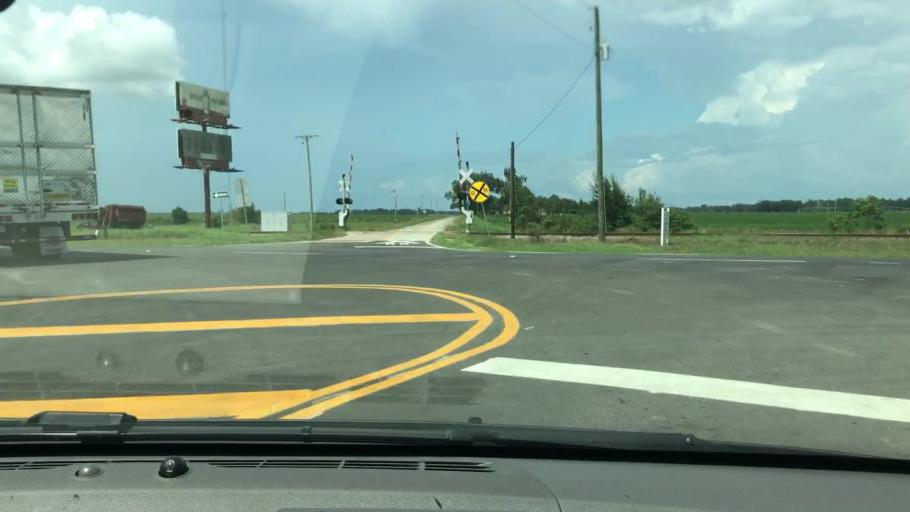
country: US
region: Georgia
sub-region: Seminole County
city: Donalsonville
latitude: 31.0919
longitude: -84.9963
